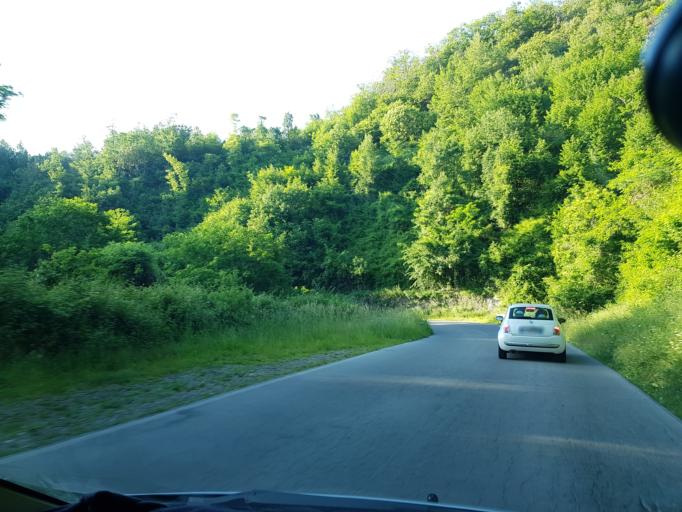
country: IT
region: Tuscany
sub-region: Provincia di Lucca
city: Minucciano
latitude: 44.1801
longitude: 10.2030
